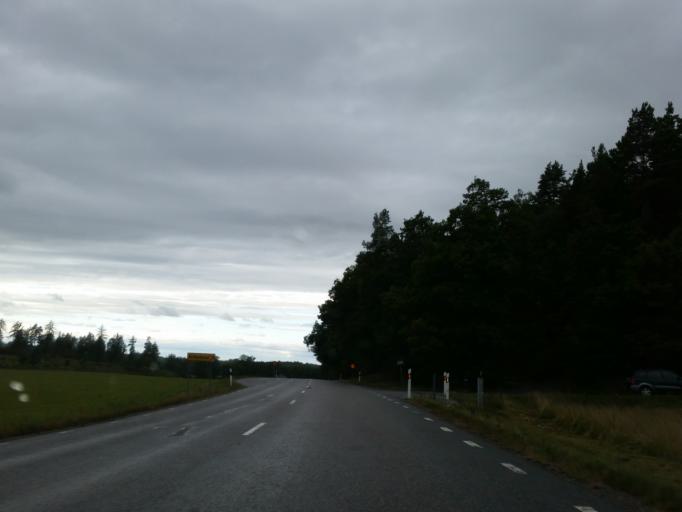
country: SE
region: Uppsala
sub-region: Habo Kommun
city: Balsta
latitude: 59.6498
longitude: 17.4216
